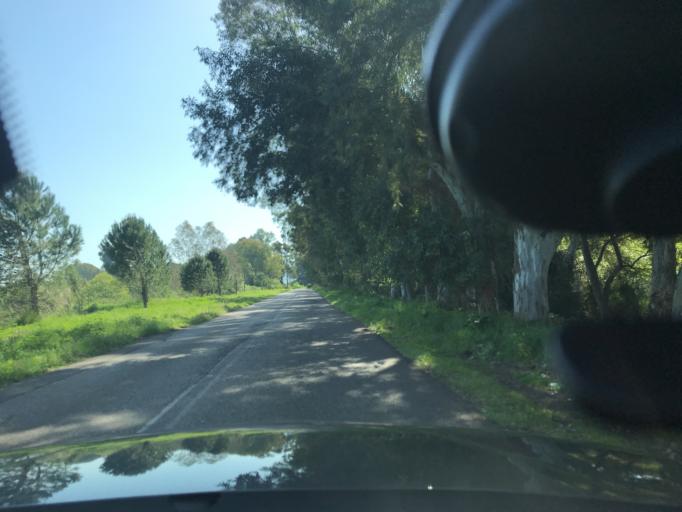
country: GR
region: West Greece
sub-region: Nomos Ileias
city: Epitalion
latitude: 37.6401
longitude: 21.4800
